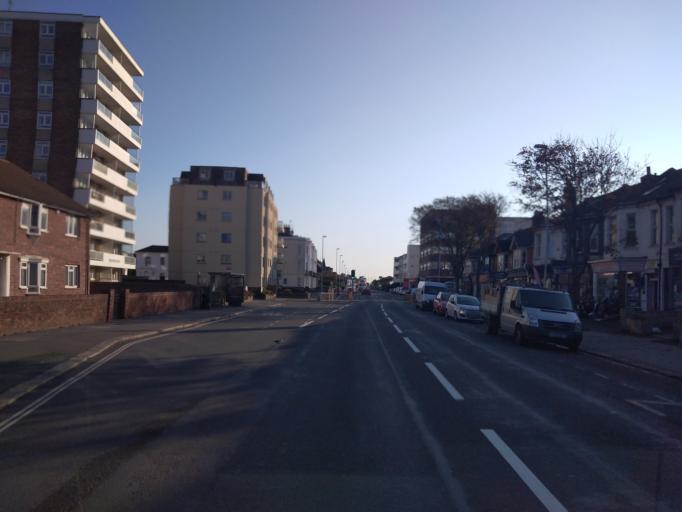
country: GB
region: England
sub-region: West Sussex
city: Worthing
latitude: 50.8125
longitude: -0.3601
